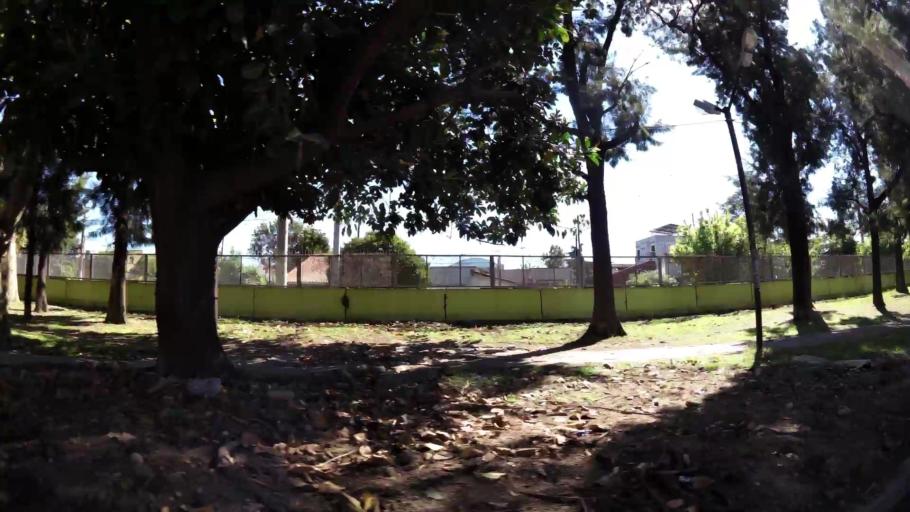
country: AR
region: Buenos Aires
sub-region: Partido de Quilmes
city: Quilmes
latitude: -34.7057
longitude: -58.2895
